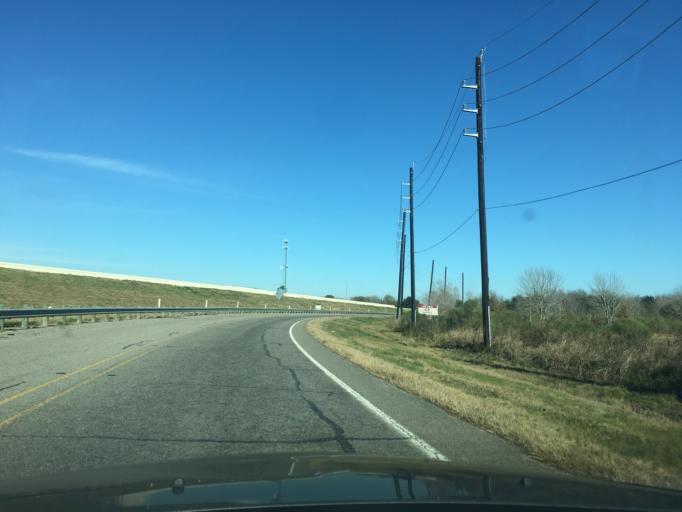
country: US
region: Texas
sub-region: Fort Bend County
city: Pleak
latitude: 29.4838
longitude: -95.9355
